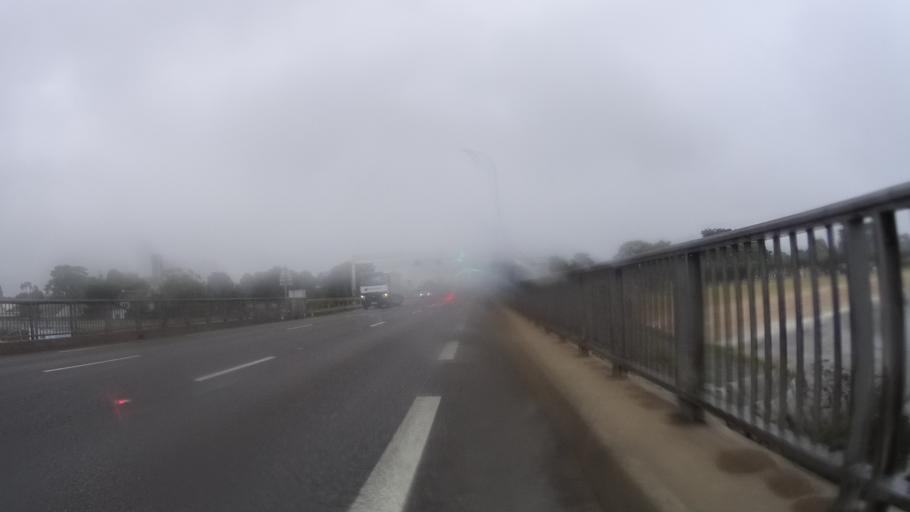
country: FR
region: Pays de la Loire
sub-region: Departement de la Loire-Atlantique
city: Saint-Brevin-les-Pins
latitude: 47.2695
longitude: -2.1623
